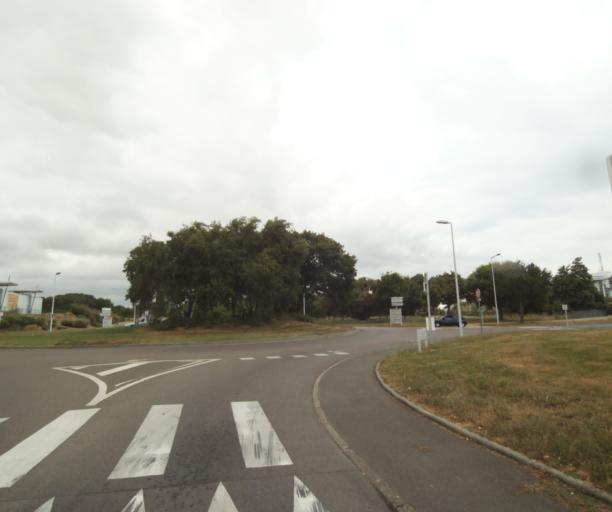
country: FR
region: Pays de la Loire
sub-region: Departement de la Vendee
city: Chateau-d'Olonne
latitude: 46.4922
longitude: -1.7462
